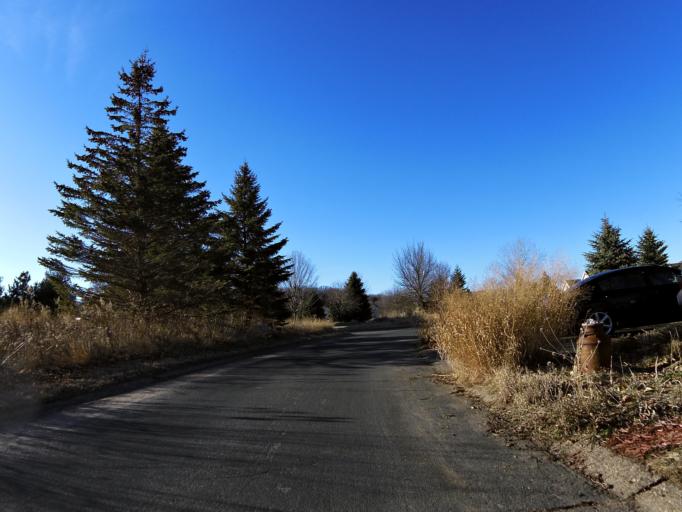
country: US
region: Minnesota
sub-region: Washington County
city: Lakeland
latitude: 44.9807
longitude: -92.7927
